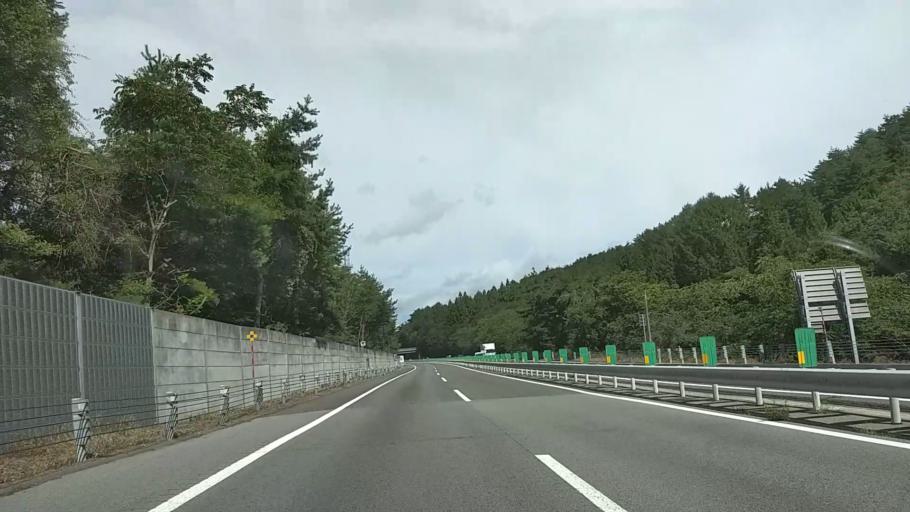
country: JP
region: Nagano
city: Chino
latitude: 35.8752
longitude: 138.3055
